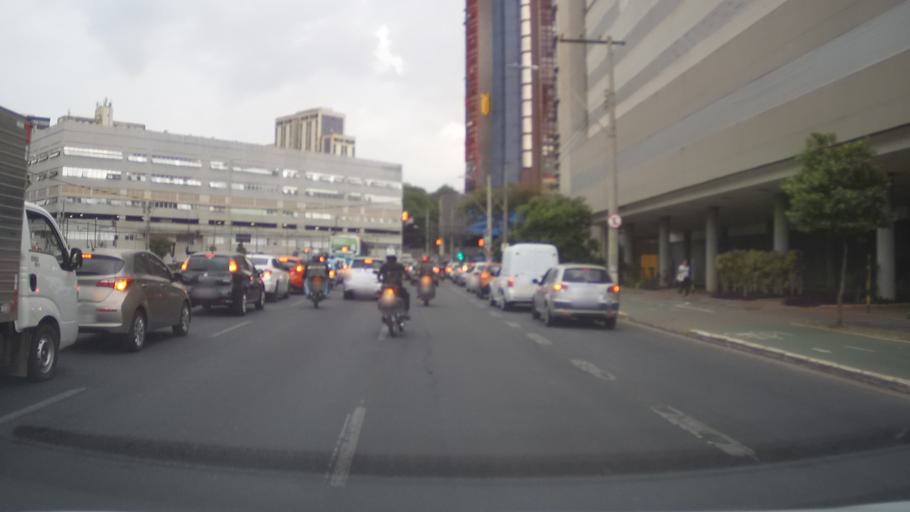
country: BR
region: Minas Gerais
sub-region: Belo Horizonte
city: Belo Horizonte
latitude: -19.9205
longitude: -43.9233
